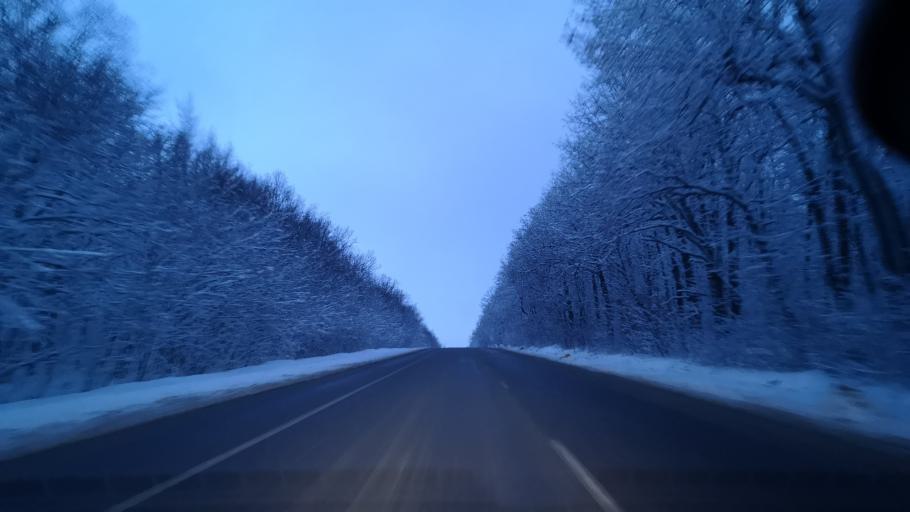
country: MD
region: Rezina
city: Rezina
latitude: 47.7253
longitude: 28.8589
